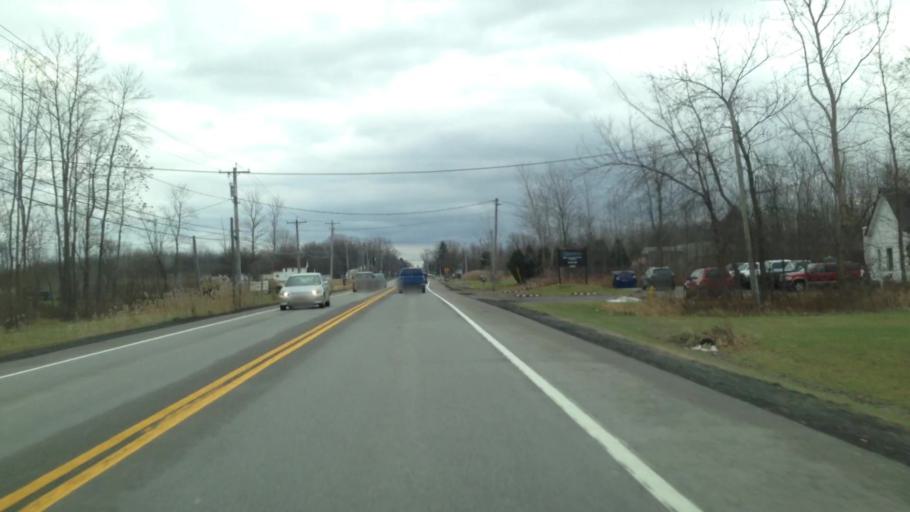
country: US
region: New York
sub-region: Erie County
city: Akron
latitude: 42.9983
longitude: -78.4835
